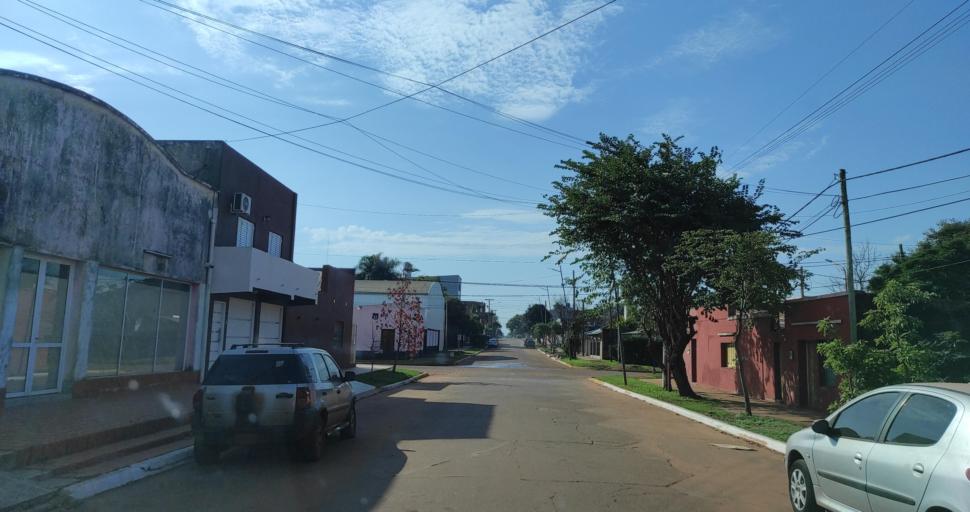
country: AR
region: Corrientes
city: Santo Tome
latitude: -28.5526
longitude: -56.0387
